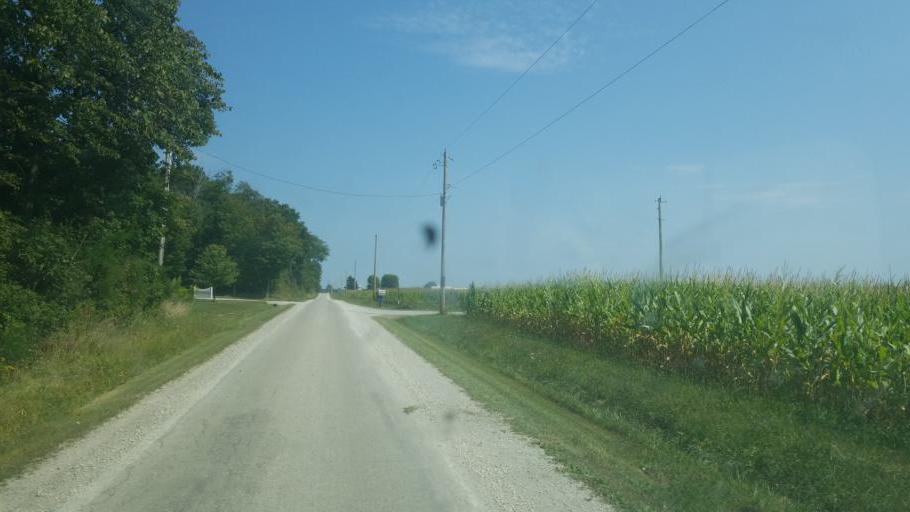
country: US
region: Ohio
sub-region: Crawford County
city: Bucyrus
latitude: 40.9361
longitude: -82.8933
